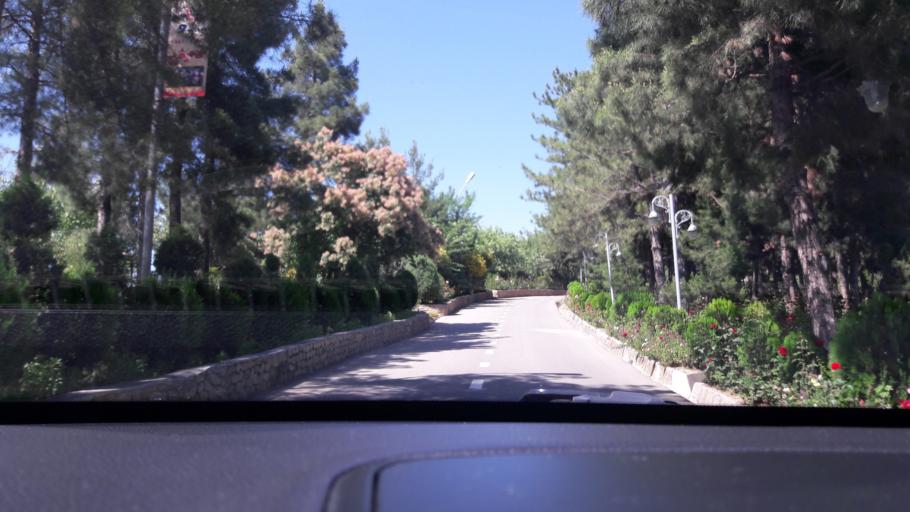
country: TJ
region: Dushanbe
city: Dushanbe
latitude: 38.5816
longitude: 68.8124
